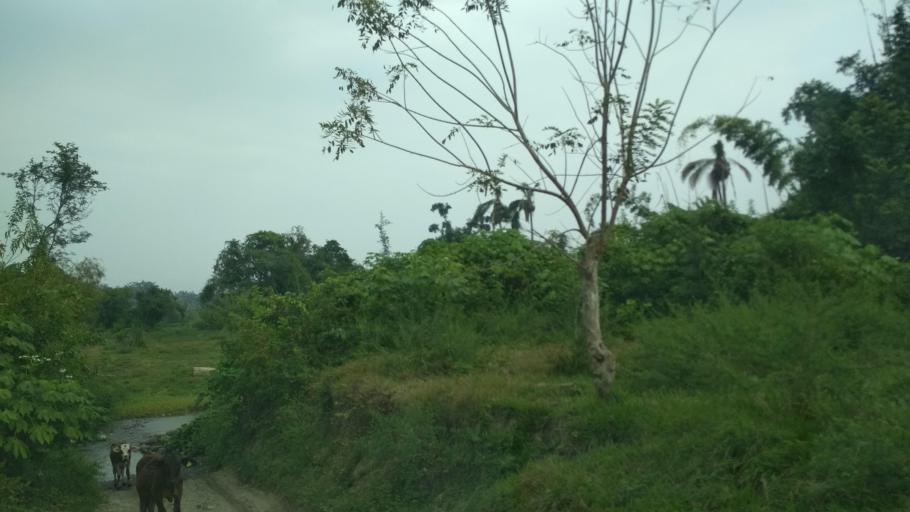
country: MM
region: Kayah
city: Loikaw
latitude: 20.2183
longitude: 97.3352
